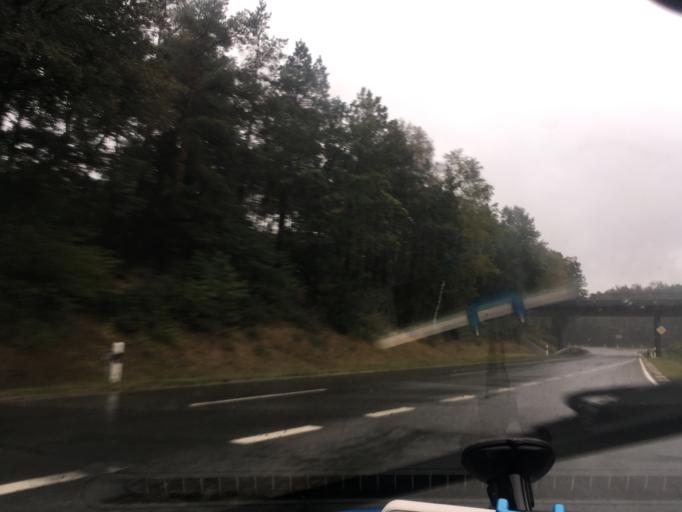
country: DE
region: Lower Saxony
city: Bispingen
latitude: 53.0617
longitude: 9.9923
